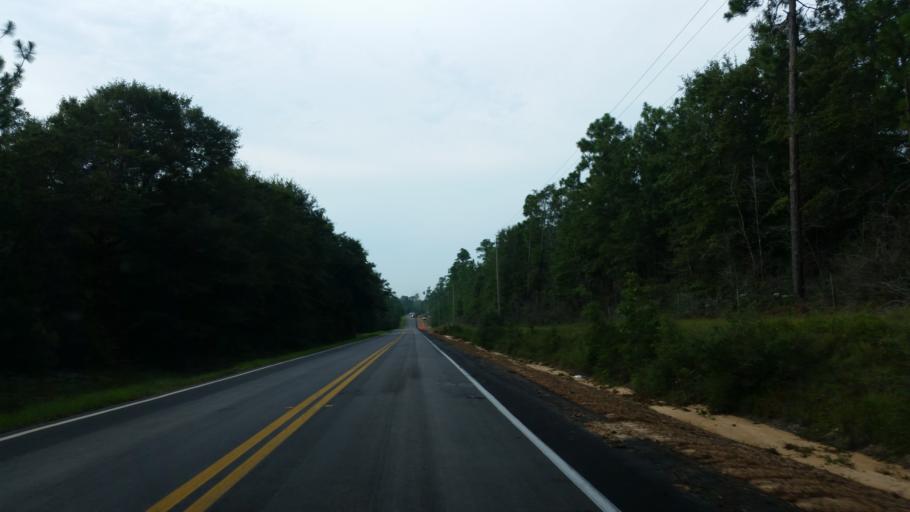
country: US
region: Florida
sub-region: Escambia County
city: Molino
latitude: 30.7665
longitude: -87.4784
